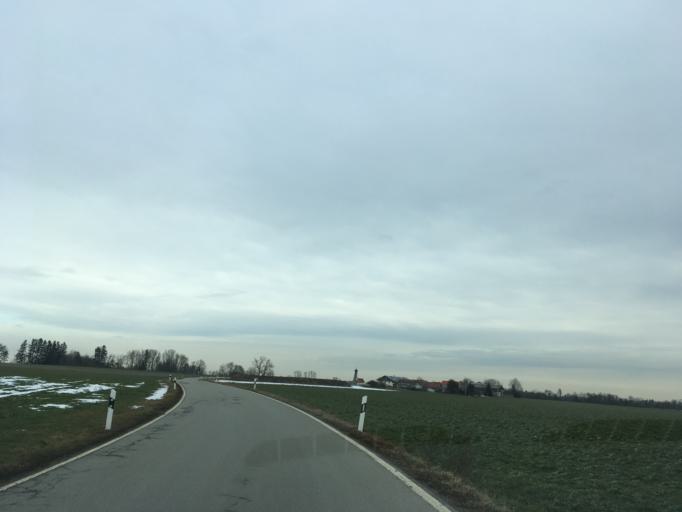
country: DE
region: Bavaria
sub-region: Upper Bavaria
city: Kraiburg am Inn
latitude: 48.1638
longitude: 12.4125
